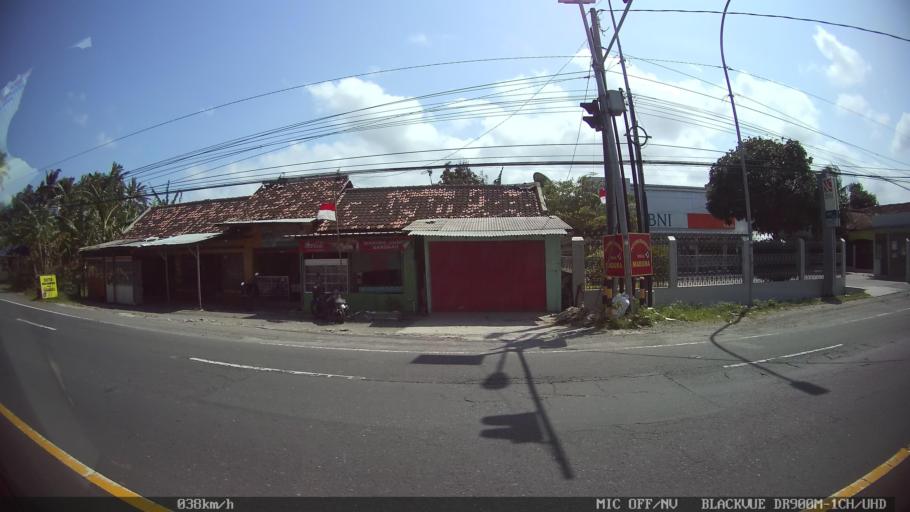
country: ID
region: Daerah Istimewa Yogyakarta
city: Srandakan
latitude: -7.8867
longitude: 110.0734
